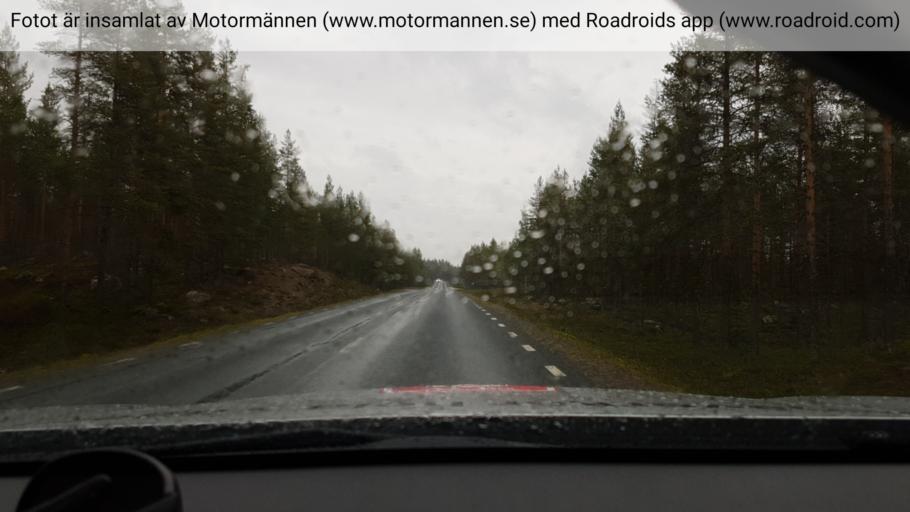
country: SE
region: Vaesterbotten
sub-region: Mala Kommun
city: Mala
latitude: 65.2155
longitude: 18.6660
